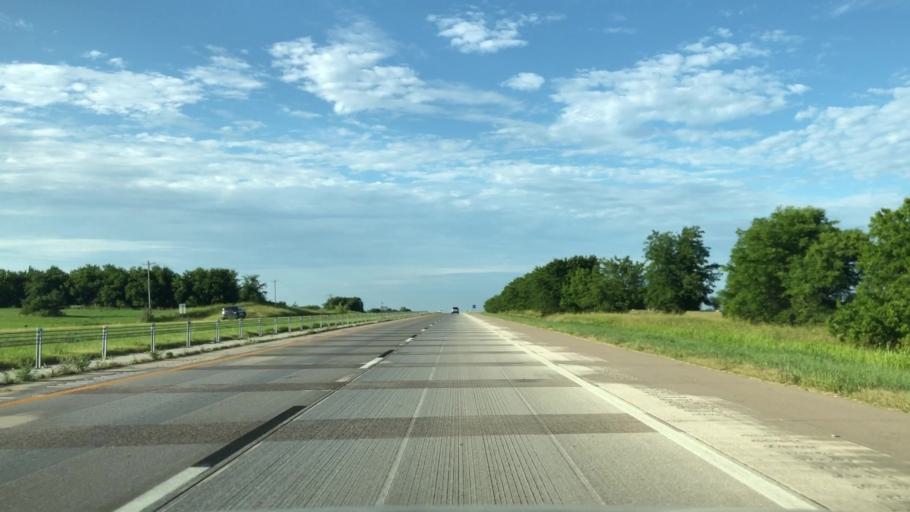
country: US
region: Oklahoma
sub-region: Osage County
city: Skiatook
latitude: 36.4294
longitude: -95.9206
